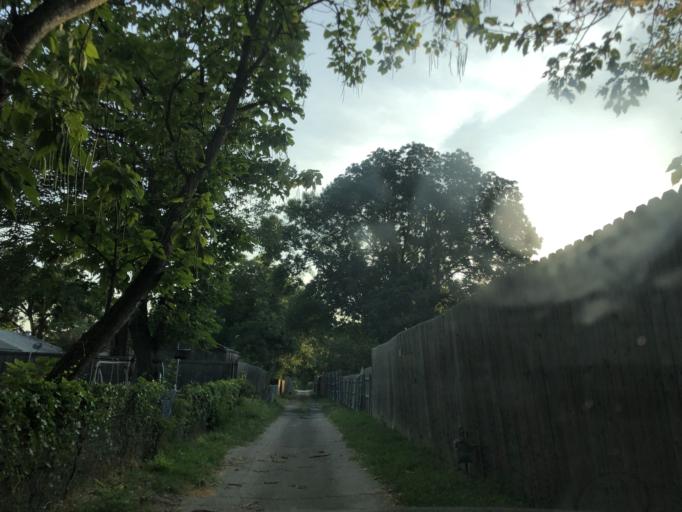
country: US
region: Texas
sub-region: Dallas County
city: Garland
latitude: 32.8600
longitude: -96.6311
